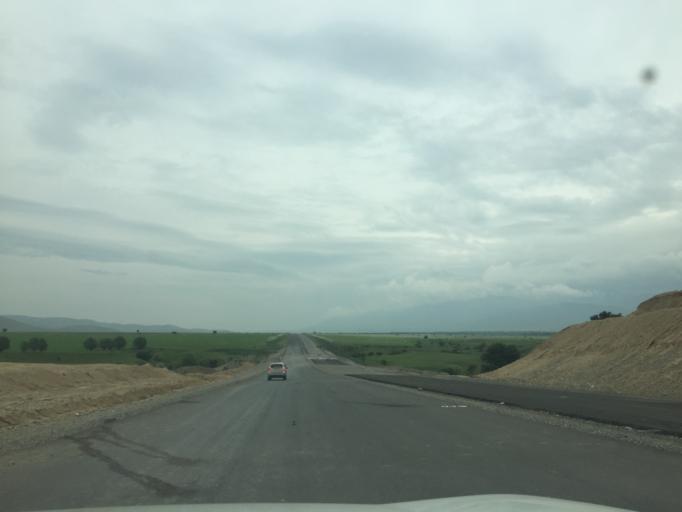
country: KZ
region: Ongtustik Qazaqstan
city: Turar Ryskulov
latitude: 42.5081
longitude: 70.4114
